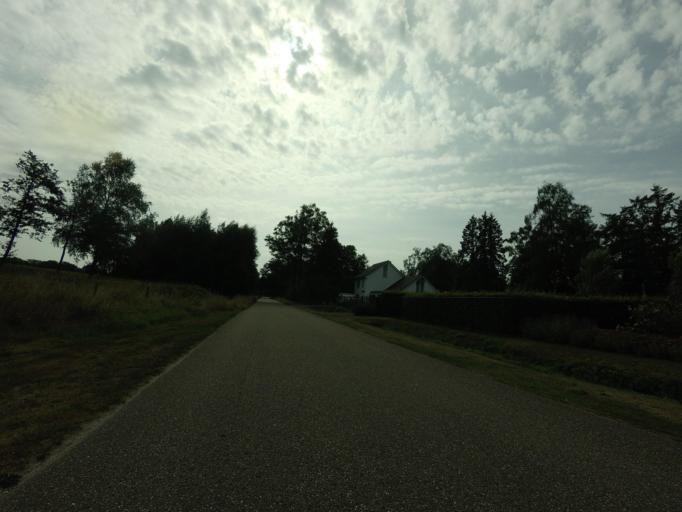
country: NL
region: North Brabant
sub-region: Gemeente Sint Anthonis
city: Sint Anthonis
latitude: 51.5703
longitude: 5.8357
